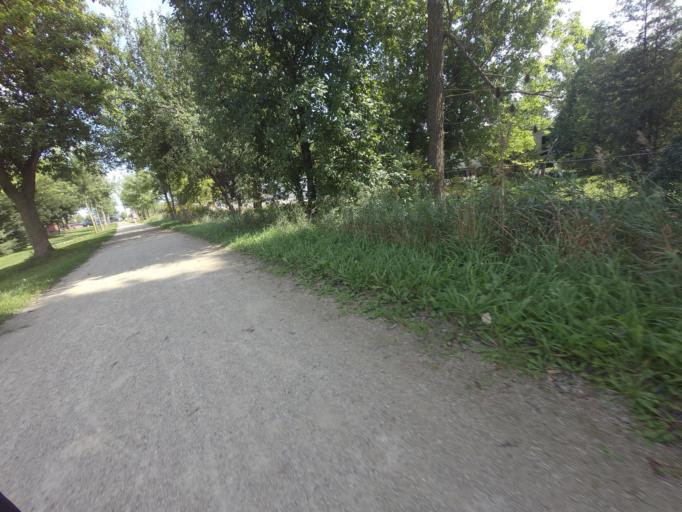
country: CA
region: Ontario
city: Waterloo
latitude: 43.5831
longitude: -80.7285
